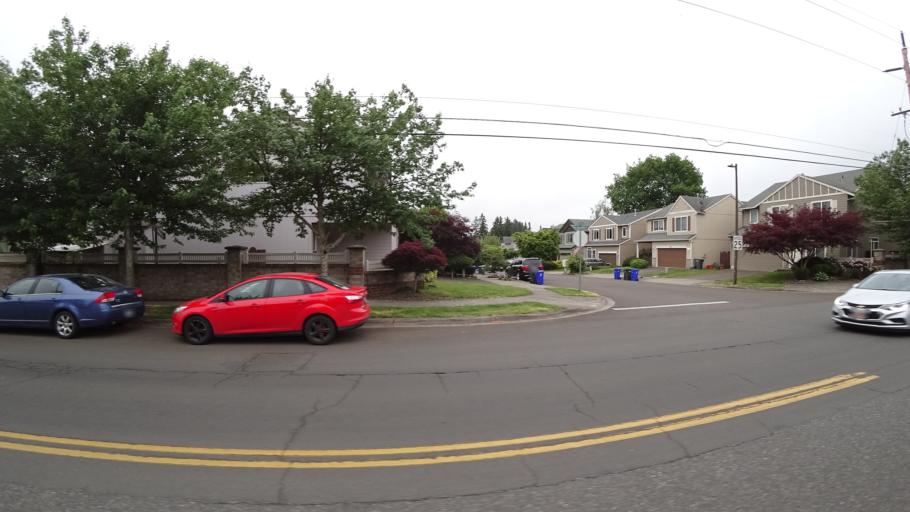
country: US
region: Oregon
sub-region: Washington County
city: Rockcreek
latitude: 45.5231
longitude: -122.9039
